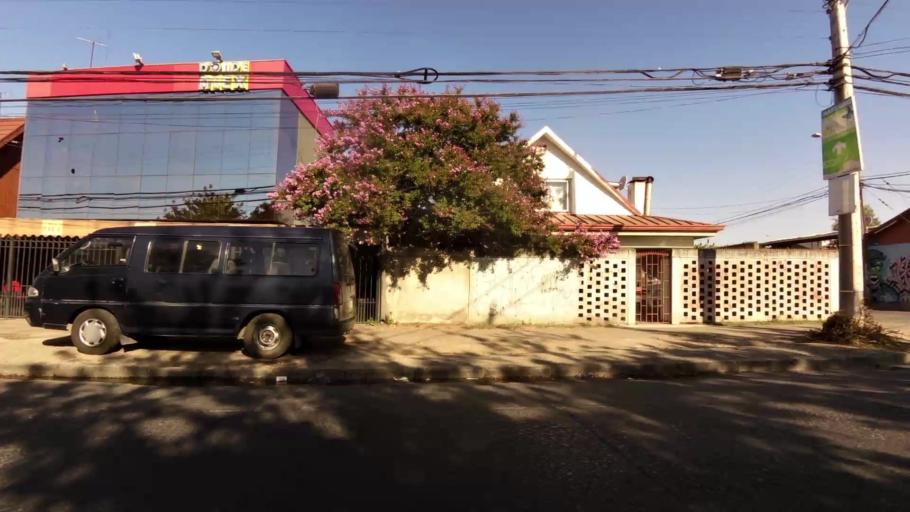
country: CL
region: Maule
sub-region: Provincia de Talca
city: Talca
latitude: -35.4438
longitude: -71.6672
